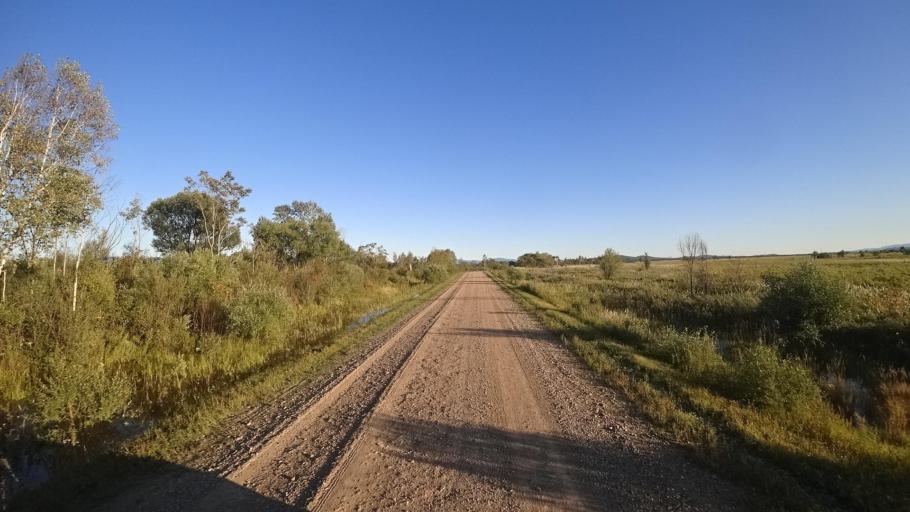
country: RU
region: Primorskiy
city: Kirovskiy
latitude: 44.8140
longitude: 133.6151
